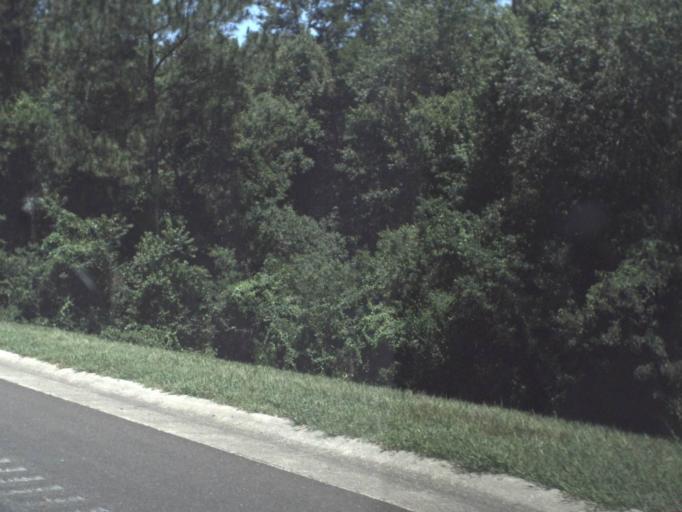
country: US
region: Florida
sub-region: Duval County
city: Jacksonville
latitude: 30.4443
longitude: -81.5999
